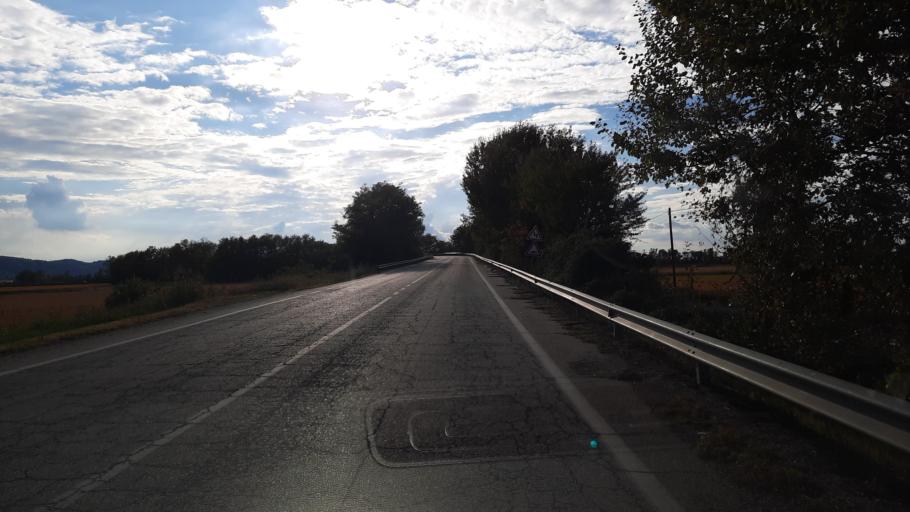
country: IT
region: Piedmont
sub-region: Provincia di Vercelli
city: Palazzolo Vercellese
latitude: 45.1926
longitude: 8.2608
